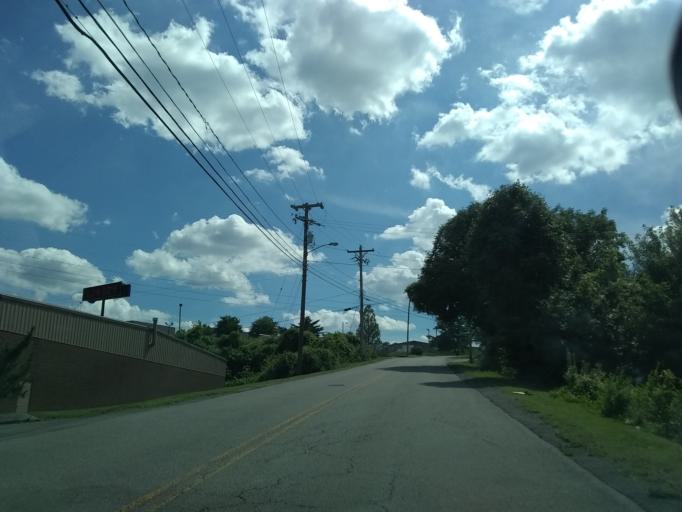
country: US
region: Tennessee
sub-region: Davidson County
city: Nashville
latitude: 36.1463
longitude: -86.6975
